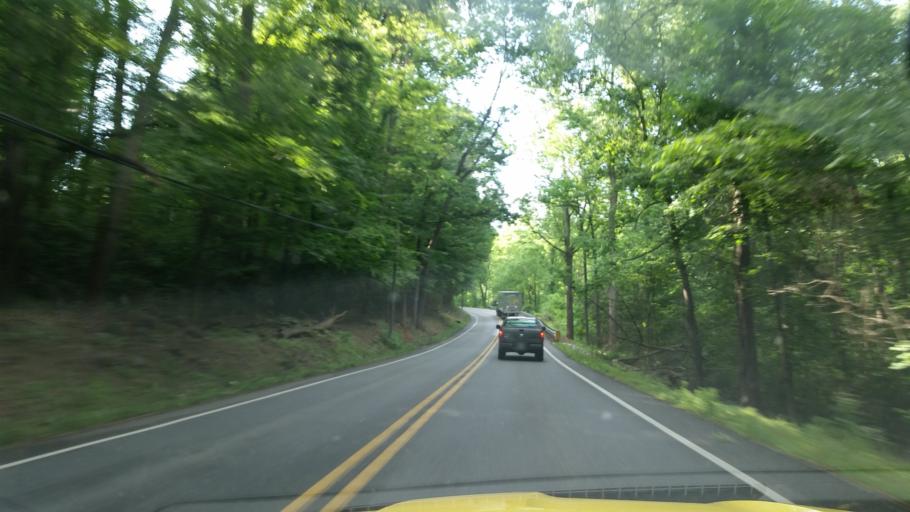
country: US
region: Pennsylvania
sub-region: Lancaster County
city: Brickerville
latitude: 40.2437
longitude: -76.2986
